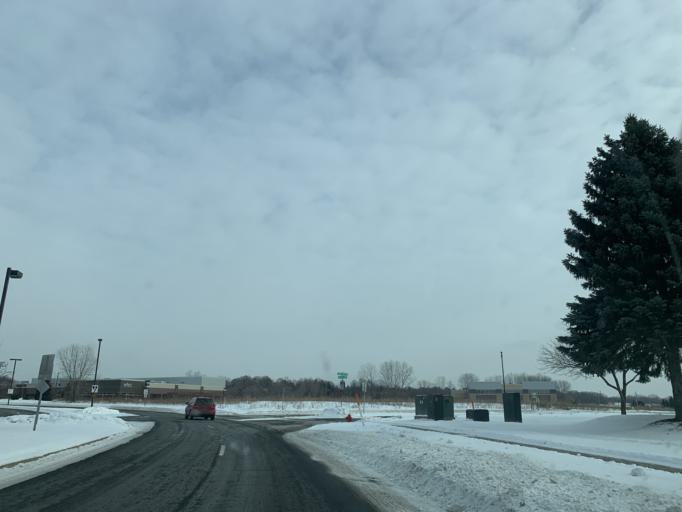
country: US
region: Minnesota
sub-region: Dakota County
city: Mendota Heights
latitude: 44.8534
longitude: -93.1252
